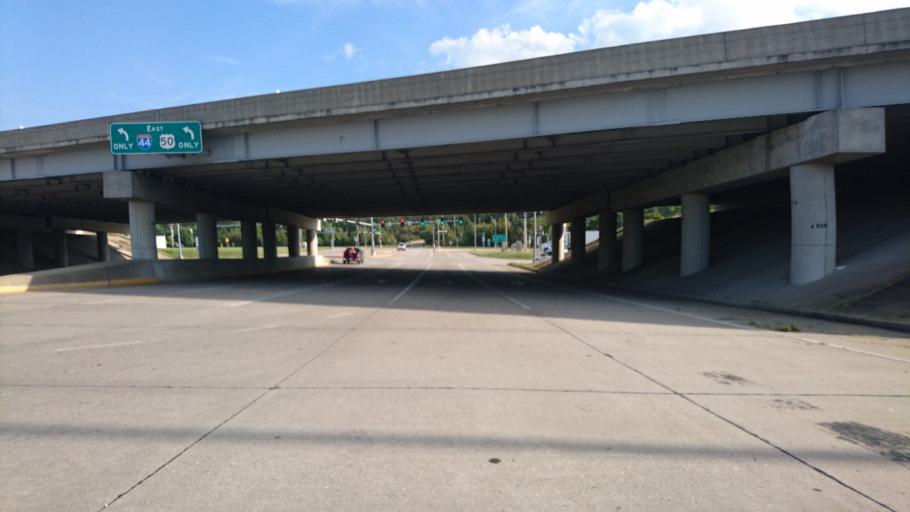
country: US
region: Missouri
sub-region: Saint Louis County
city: Eureka
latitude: 38.5061
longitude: -90.6777
